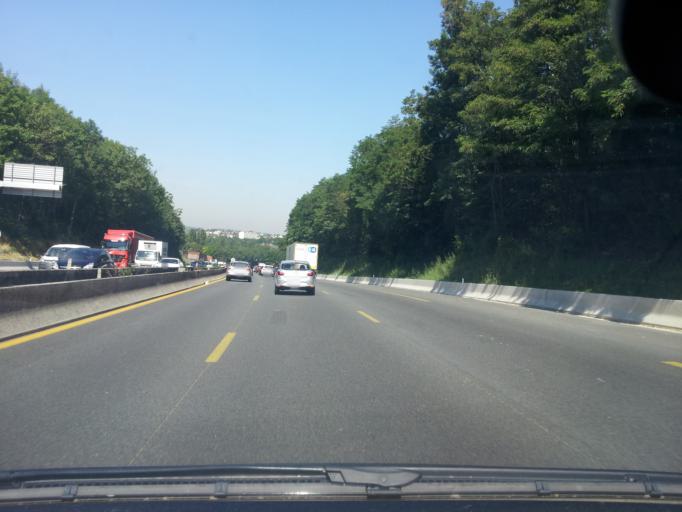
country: FR
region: Ile-de-France
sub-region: Departement de l'Essonne
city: Morsang-sur-Orge
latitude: 48.6675
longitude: 2.3588
